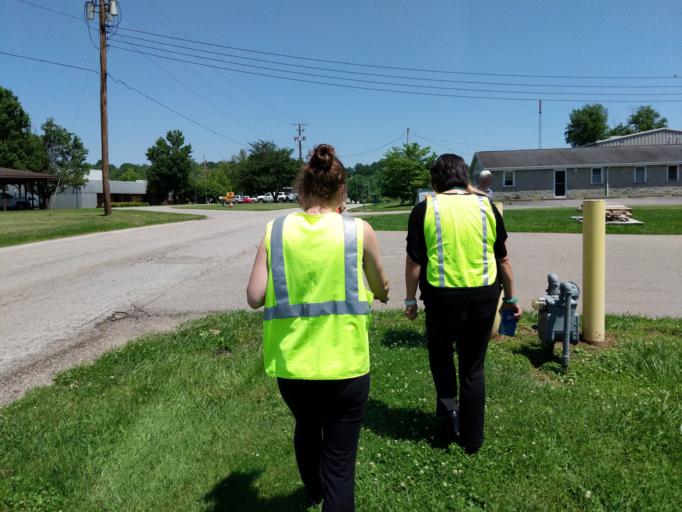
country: US
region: Ohio
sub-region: Washington County
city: Reno
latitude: 39.3937
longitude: -81.4044
